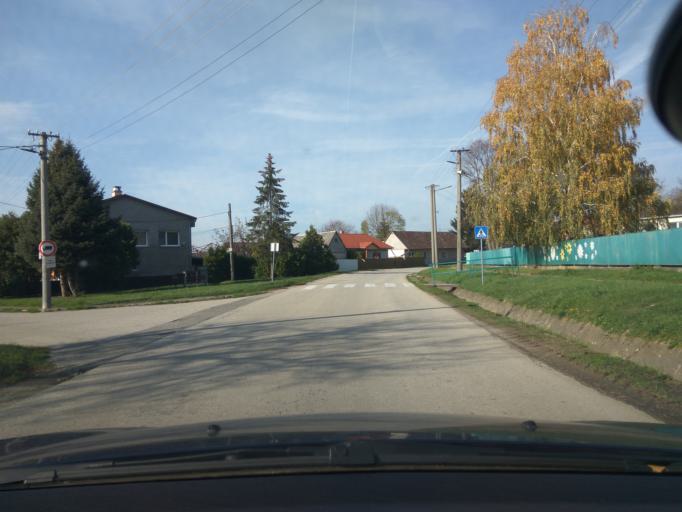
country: SK
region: Trnavsky
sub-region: Okres Senica
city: Senica
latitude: 48.6222
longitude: 17.4426
